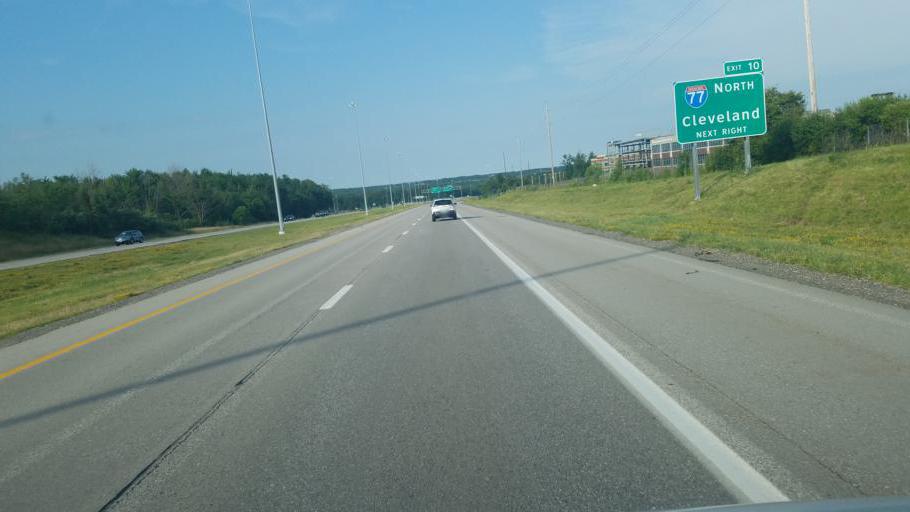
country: US
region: Ohio
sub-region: Summit County
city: Richfield
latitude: 41.2240
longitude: -81.6369
